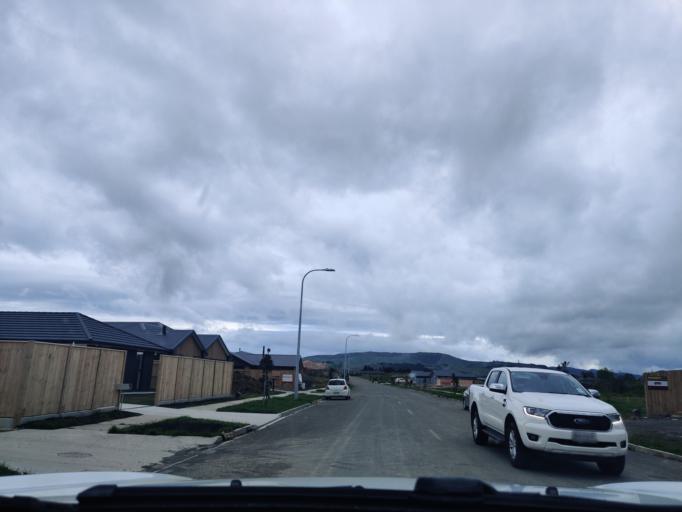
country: NZ
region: Manawatu-Wanganui
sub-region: Palmerston North City
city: Palmerston North
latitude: -40.3876
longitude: 175.6472
